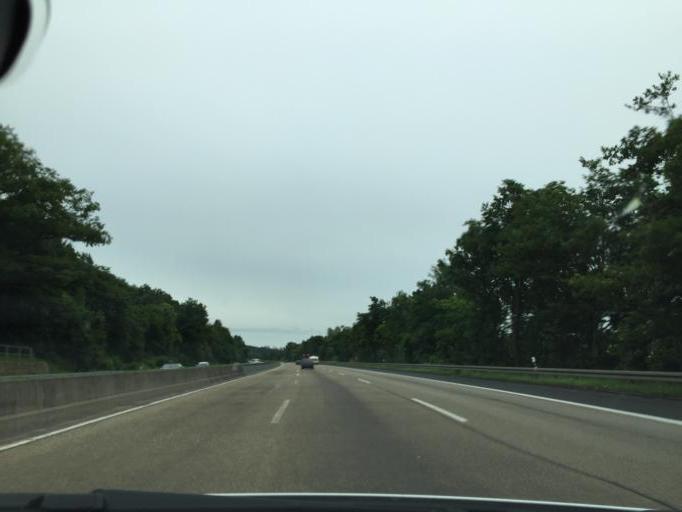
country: DE
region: Bavaria
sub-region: Regierungsbezirk Unterfranken
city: Motten
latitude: 50.4002
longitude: 9.7309
